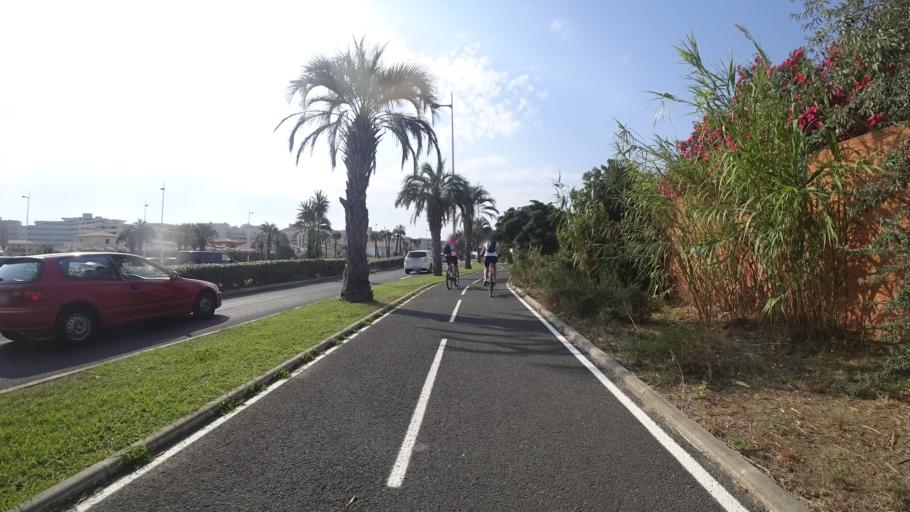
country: FR
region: Languedoc-Roussillon
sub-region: Departement des Pyrenees-Orientales
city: Canet-en-Roussillon
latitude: 42.6773
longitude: 3.0301
